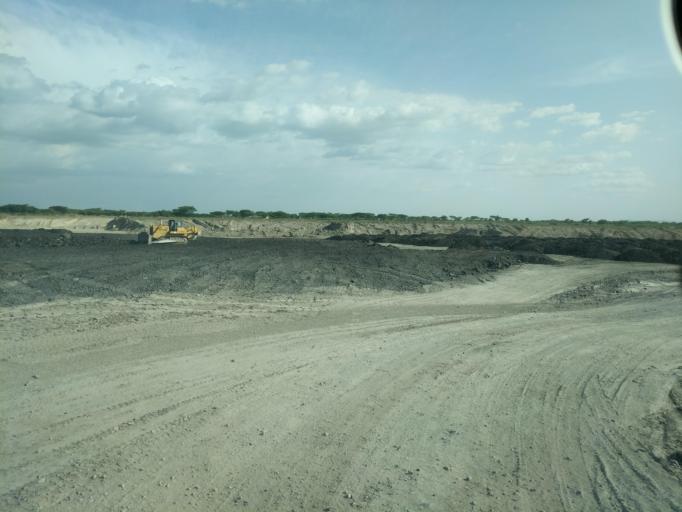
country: ET
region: Oromiya
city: Ziway
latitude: 7.5822
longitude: 38.6823
